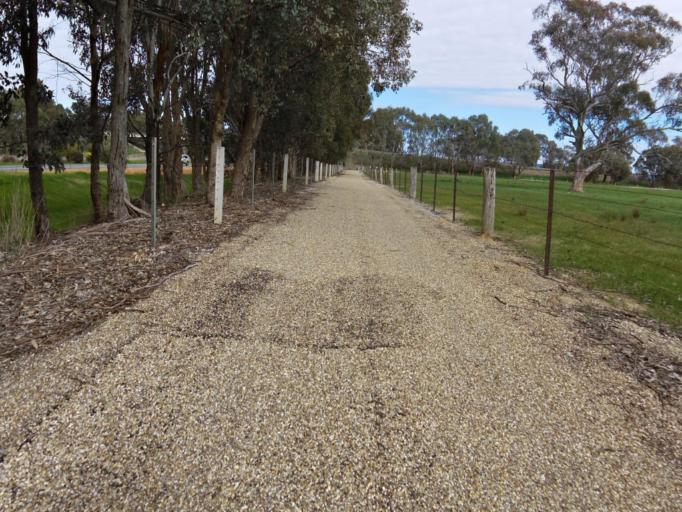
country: AU
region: Victoria
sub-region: Wangaratta
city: Wangaratta
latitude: -36.3924
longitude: 146.3408
